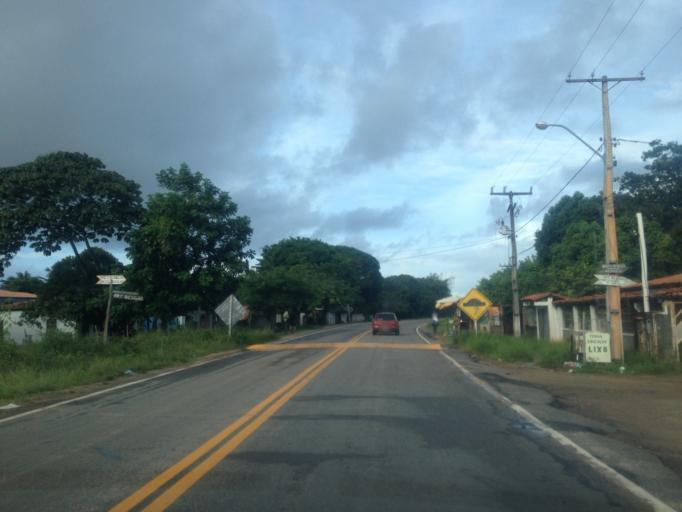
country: BR
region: Bahia
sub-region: Mata De Sao Joao
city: Mata de Sao Joao
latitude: -12.3759
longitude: -37.8928
